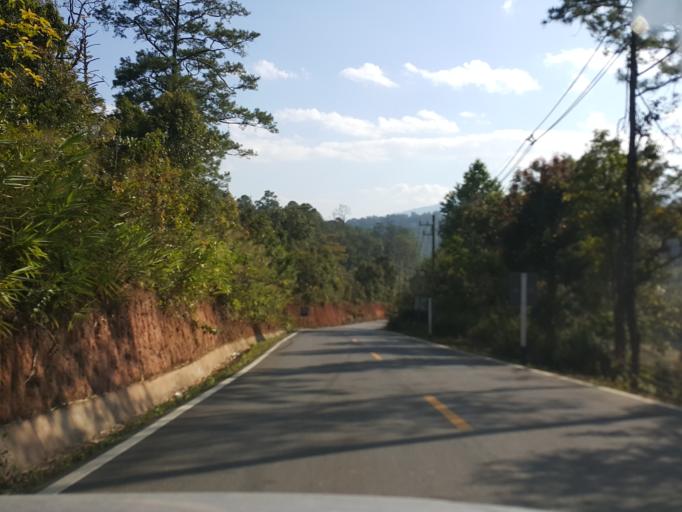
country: TH
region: Chiang Mai
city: Mae Wang
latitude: 18.6682
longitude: 98.5505
